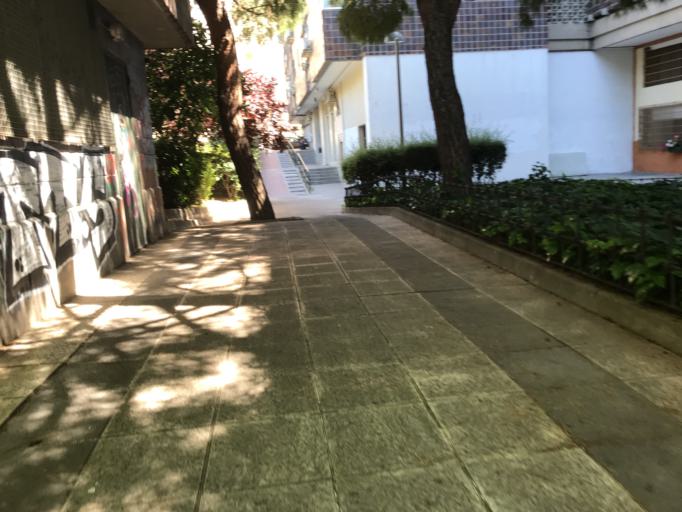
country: ES
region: Madrid
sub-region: Provincia de Madrid
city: Retiro
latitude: 40.4156
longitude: -3.6731
